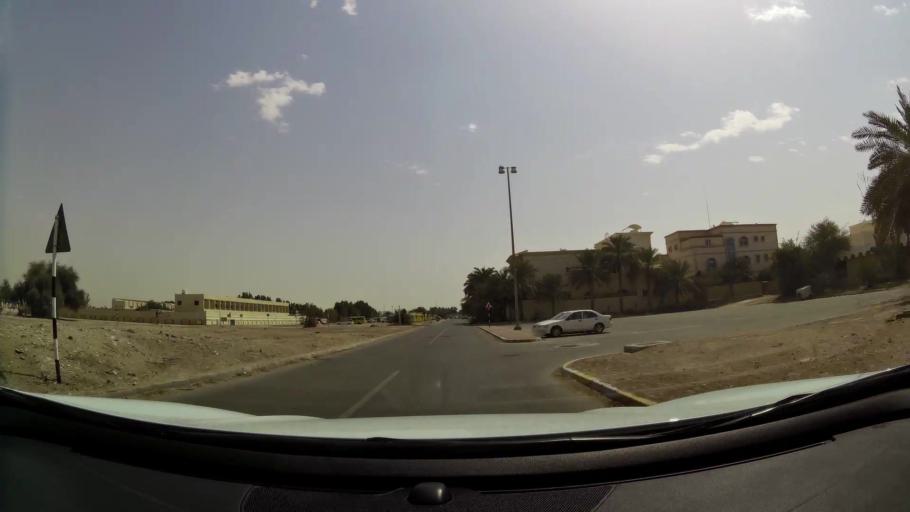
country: AE
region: Abu Dhabi
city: Abu Dhabi
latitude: 24.2922
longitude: 54.6368
